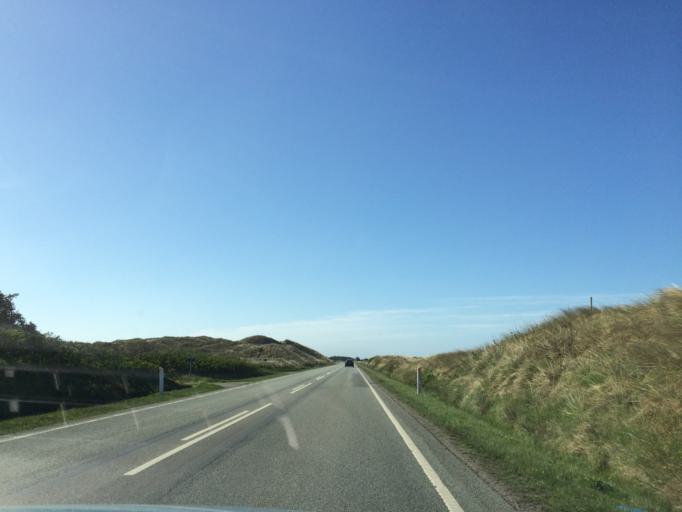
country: DK
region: Central Jutland
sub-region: Ringkobing-Skjern Kommune
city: Hvide Sande
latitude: 55.9600
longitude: 8.1467
